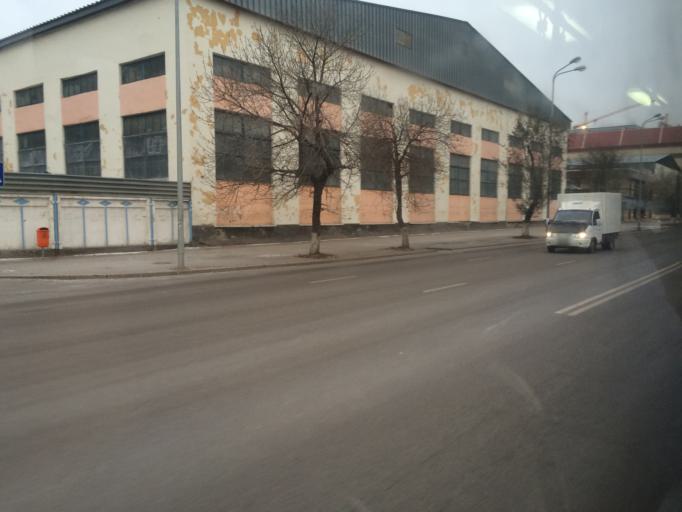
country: KZ
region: Astana Qalasy
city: Astana
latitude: 51.1713
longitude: 71.4387
